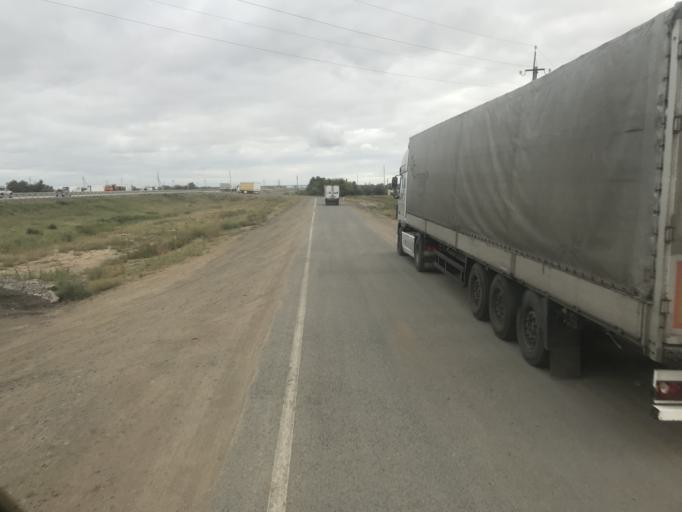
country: KZ
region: Pavlodar
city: Qalqaman
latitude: 51.9504
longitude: 75.9855
